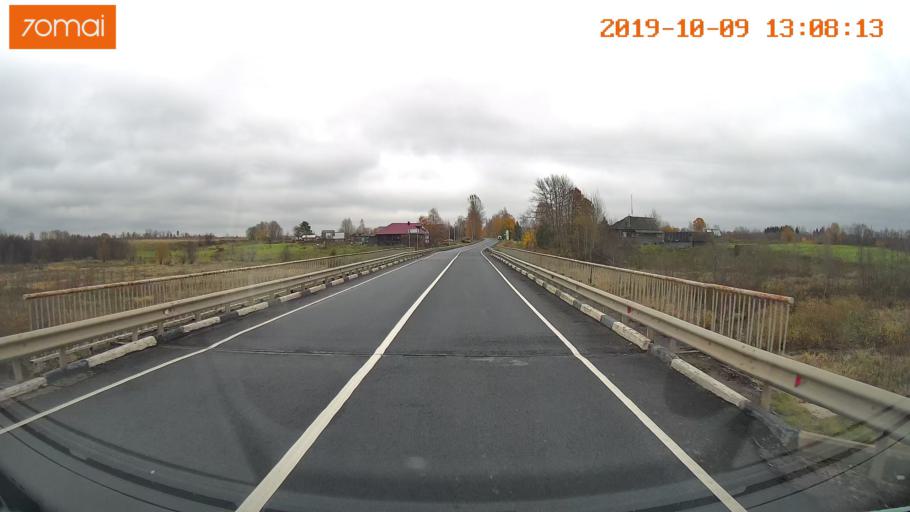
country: RU
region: Jaroslavl
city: Lyubim
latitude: 58.3562
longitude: 40.6602
